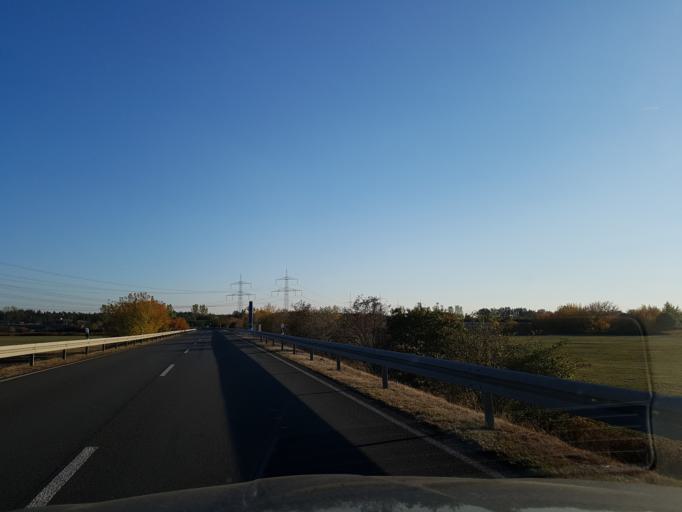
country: DE
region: Brandenburg
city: Bad Liebenwerda
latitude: 51.5175
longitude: 13.4264
